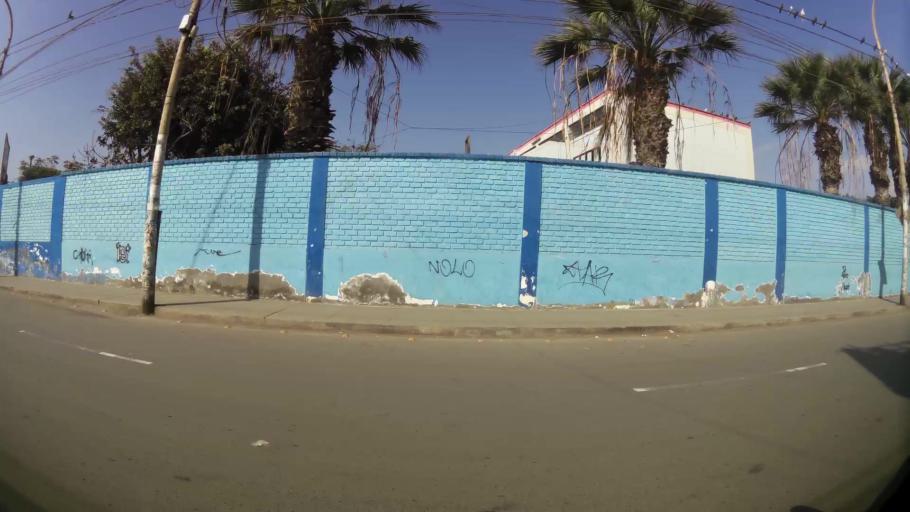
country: PE
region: Lima
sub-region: Huaura
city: Huacho
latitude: -11.1218
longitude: -77.6107
